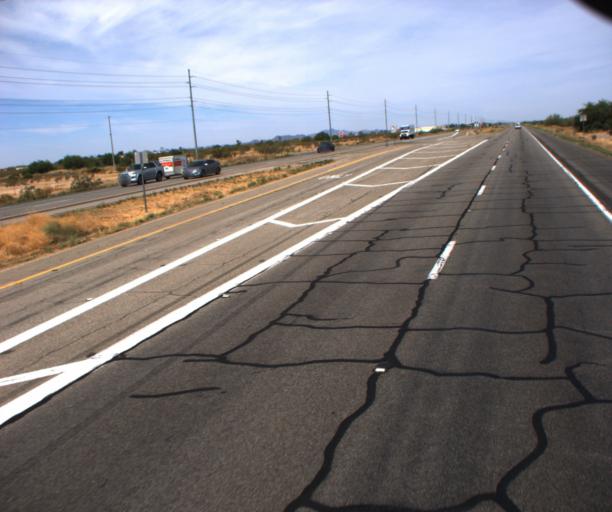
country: US
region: Arizona
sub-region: Maricopa County
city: Sun City West
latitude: 33.7613
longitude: -112.5072
